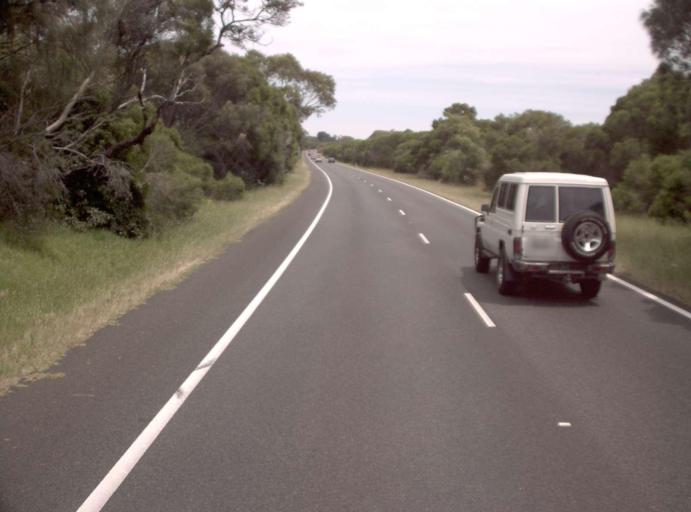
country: AU
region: Victoria
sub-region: Mornington Peninsula
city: McCrae
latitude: -38.3601
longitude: 144.9212
